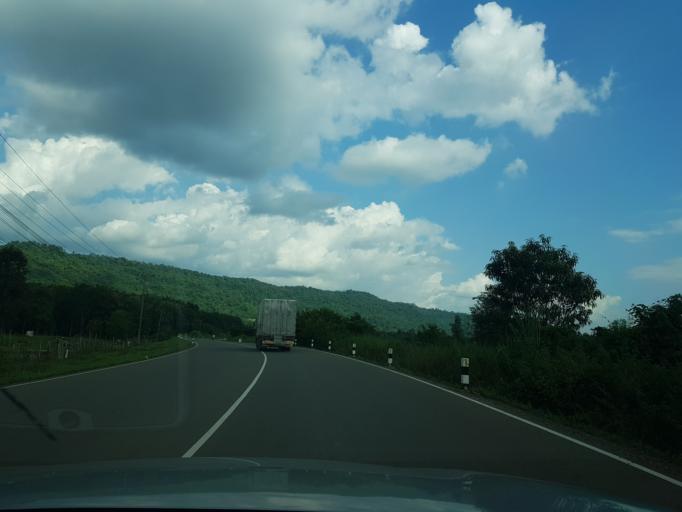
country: TH
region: Nong Khai
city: Sangkhom
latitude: 18.0247
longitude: 102.3798
